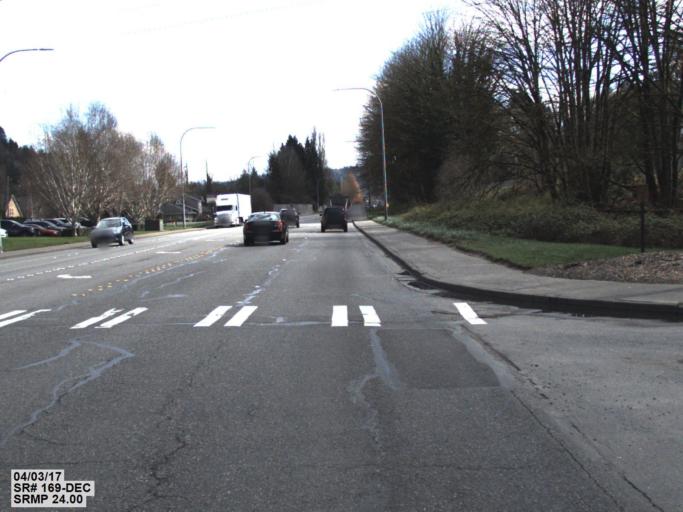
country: US
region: Washington
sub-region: King County
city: Fairwood
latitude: 47.4754
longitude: -122.1753
